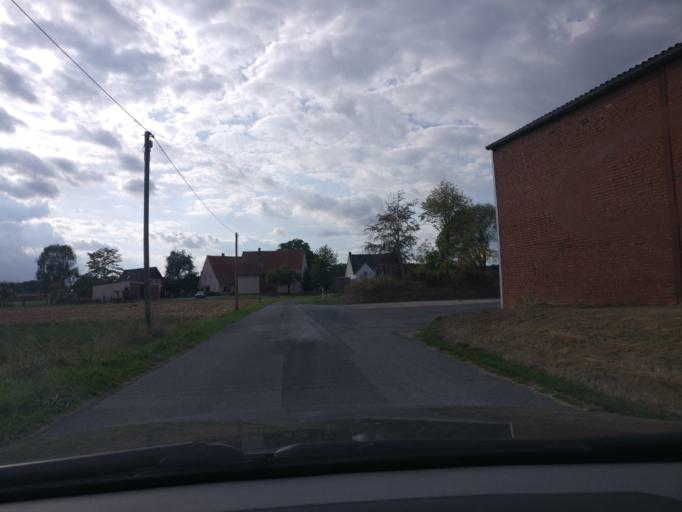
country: DE
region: Lower Saxony
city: Neuenkirchen
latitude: 52.1719
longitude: 8.3665
